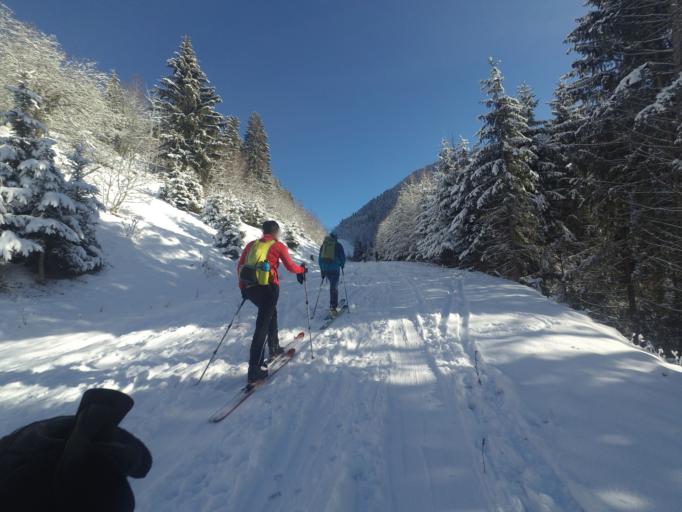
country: AT
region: Salzburg
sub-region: Politischer Bezirk Sankt Johann im Pongau
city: Sankt Johann im Pongau
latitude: 47.3179
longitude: 13.2096
